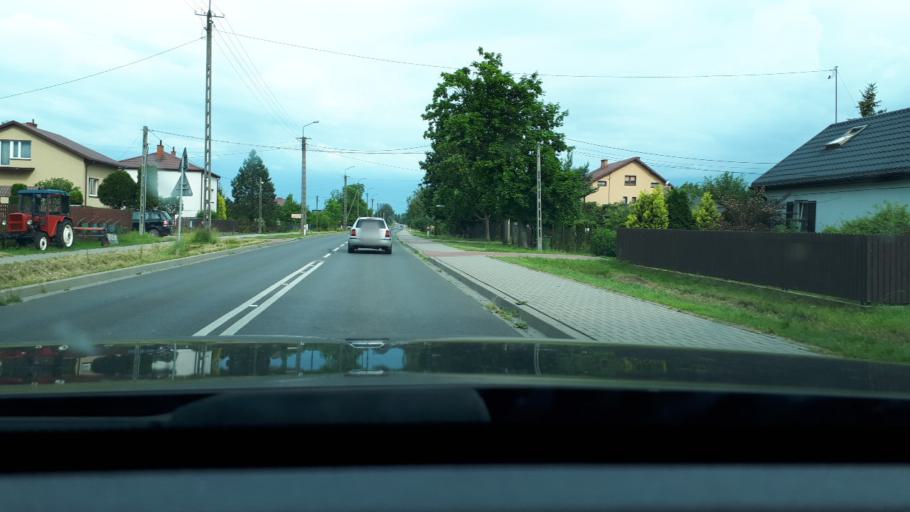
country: PL
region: Masovian Voivodeship
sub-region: Powiat warszawski zachodni
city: Kampinos
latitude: 52.2664
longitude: 20.4721
